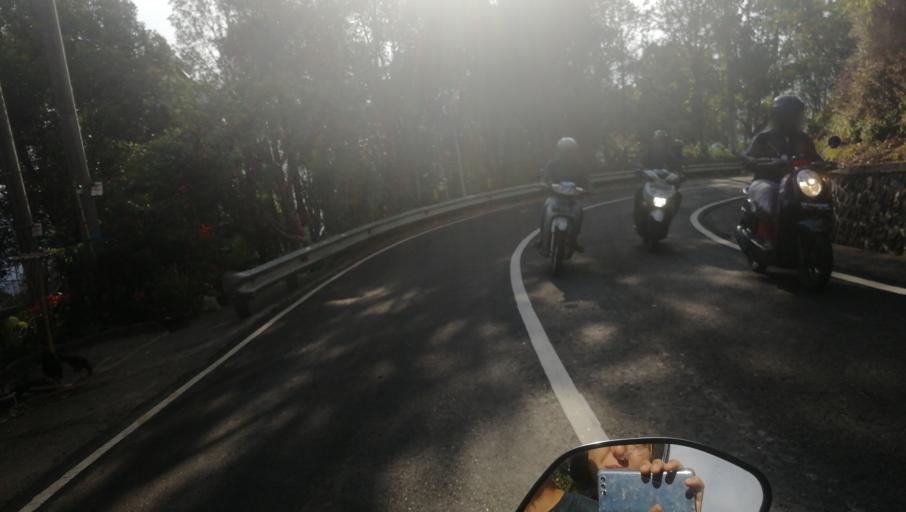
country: ID
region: Bali
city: Munduk
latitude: -8.2613
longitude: 115.0715
